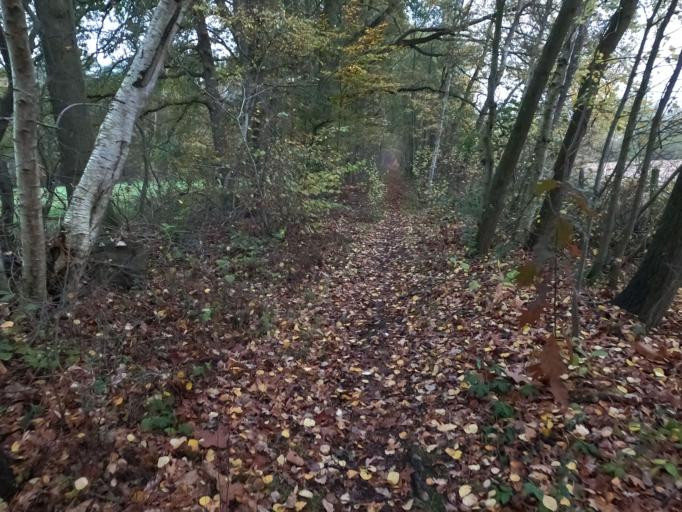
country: BE
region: Flanders
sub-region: Provincie Antwerpen
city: Nijlen
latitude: 51.1346
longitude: 4.7027
